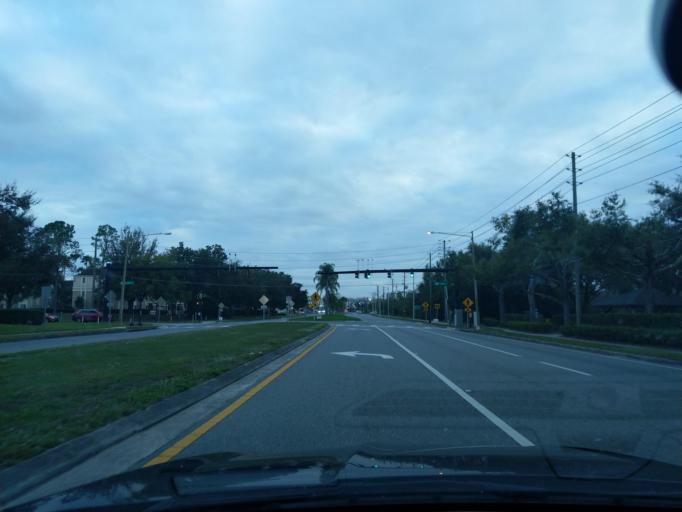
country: US
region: Florida
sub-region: Orange County
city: Doctor Phillips
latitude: 28.3920
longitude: -81.5062
